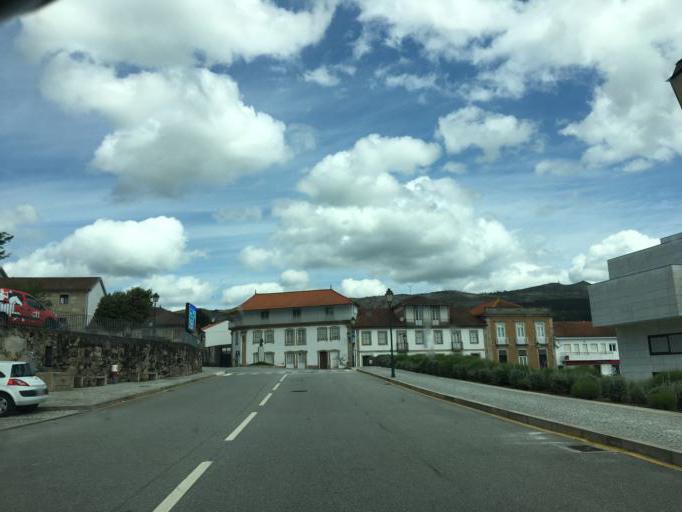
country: PT
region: Vila Real
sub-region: Boticas
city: Boticas
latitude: 41.6869
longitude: -7.6684
